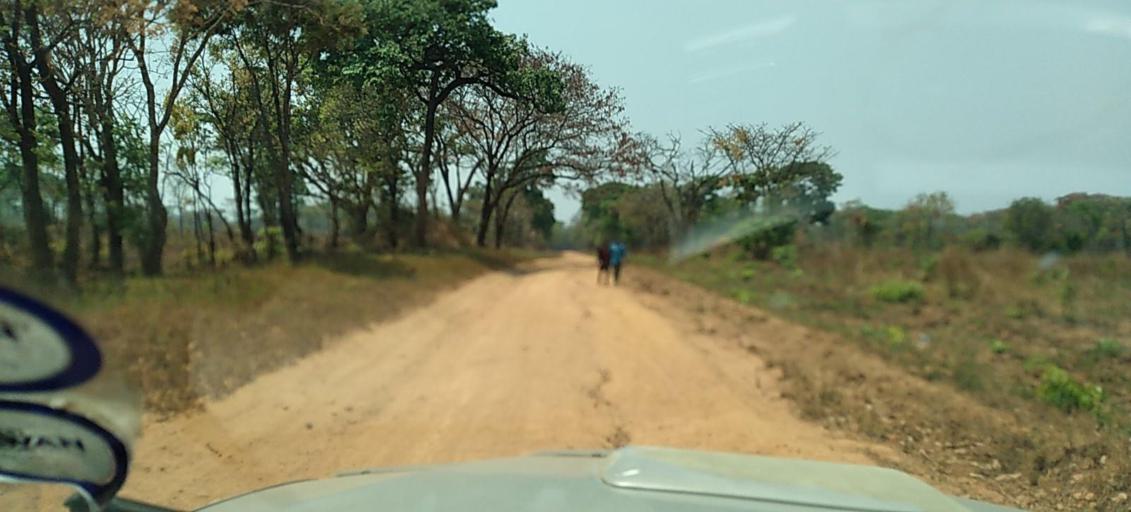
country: ZM
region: North-Western
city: Kasempa
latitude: -13.5447
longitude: 26.0432
